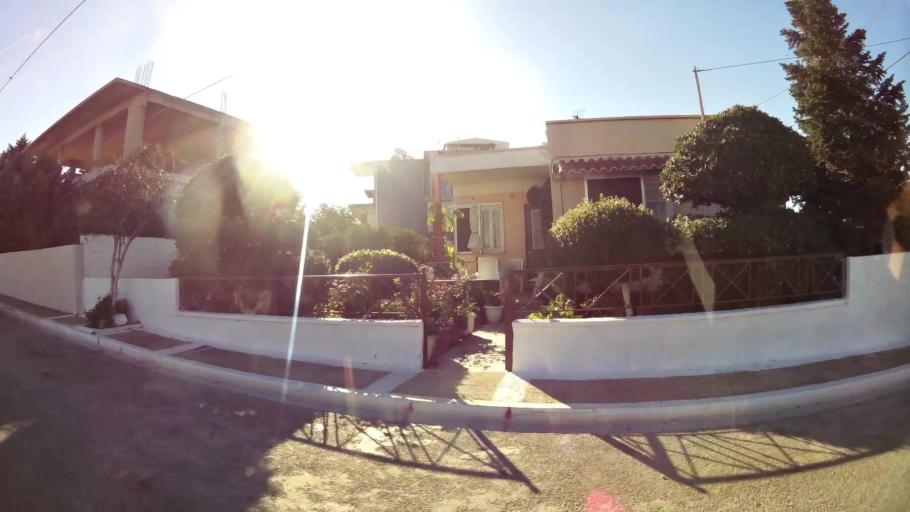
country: GR
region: Attica
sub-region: Nomarchia Anatolikis Attikis
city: Kalyvia Thorikou
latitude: 37.8378
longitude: 23.9245
